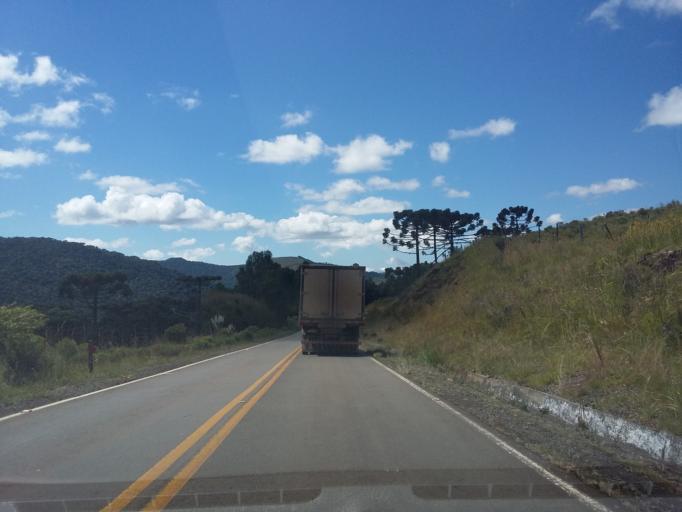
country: BR
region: Santa Catarina
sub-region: Sao Joaquim
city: Sao Joaquim
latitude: -28.2966
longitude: -49.7370
